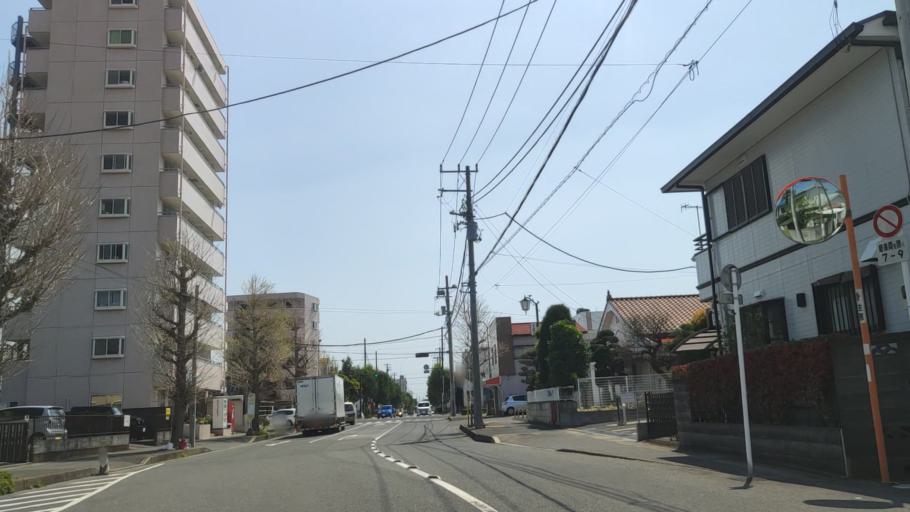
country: JP
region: Kanagawa
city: Hiratsuka
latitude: 35.3316
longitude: 139.3359
